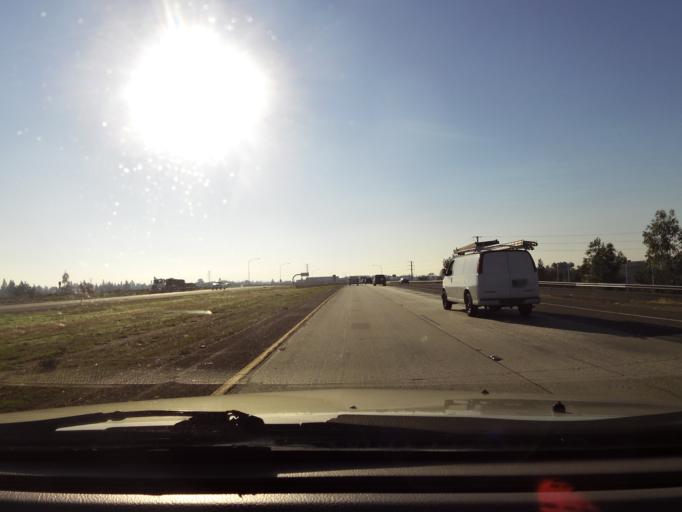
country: US
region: California
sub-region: Fresno County
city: Clovis
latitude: 36.8537
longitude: -119.7885
